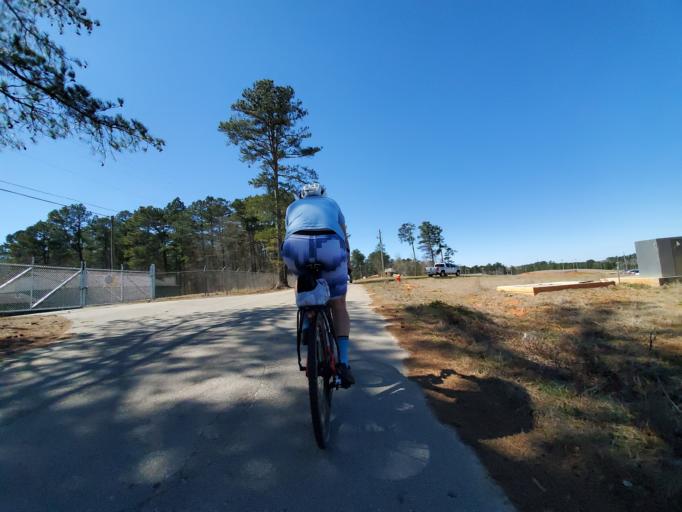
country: US
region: Georgia
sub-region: Barrow County
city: Russell
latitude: 33.9756
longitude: -83.7147
